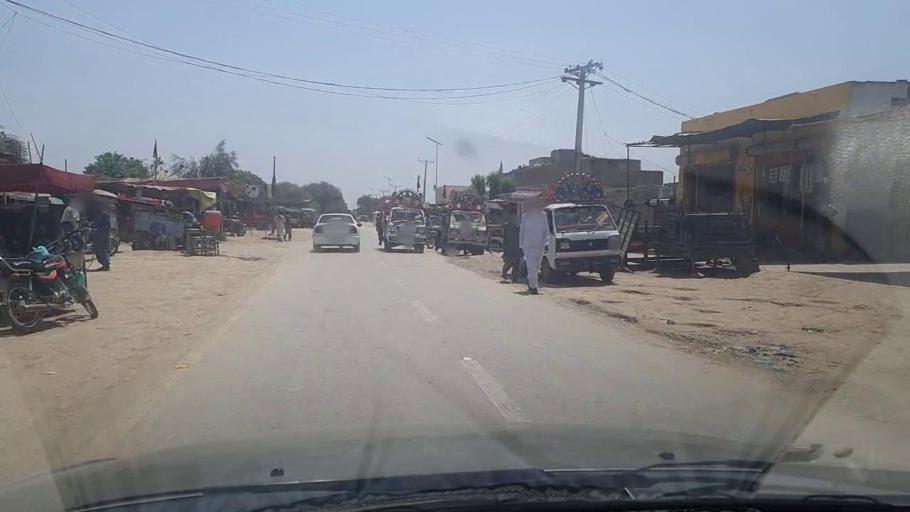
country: PK
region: Sindh
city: Tando Jam
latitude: 25.3089
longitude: 68.5748
